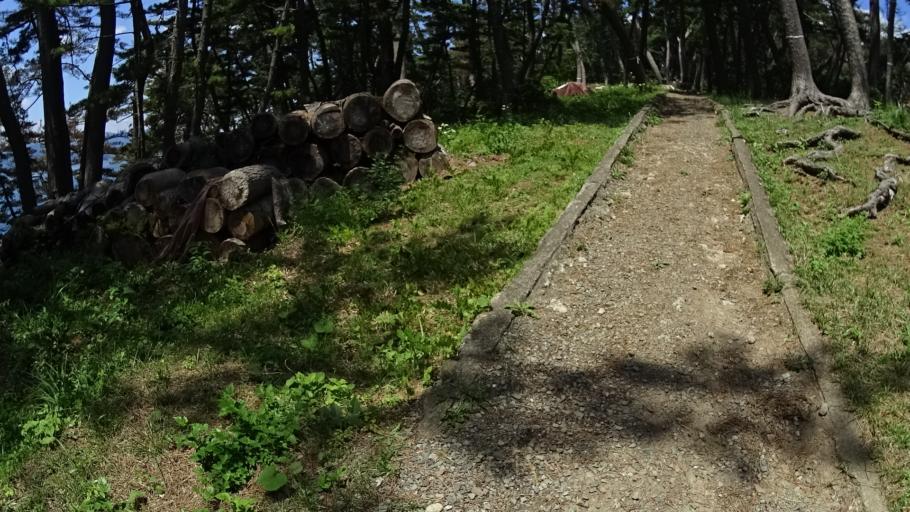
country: JP
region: Iwate
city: Ofunato
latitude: 38.8324
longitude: 141.6239
